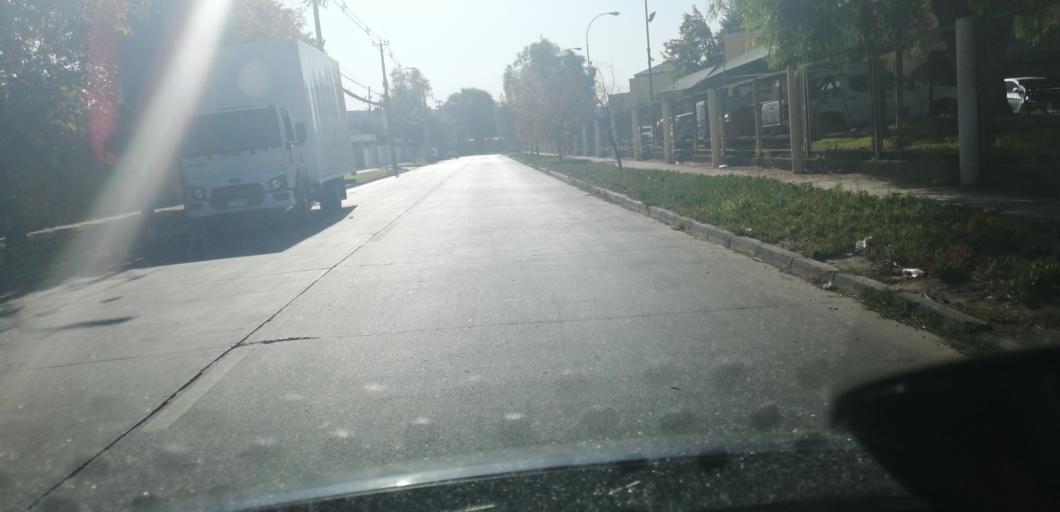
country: CL
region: Santiago Metropolitan
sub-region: Provincia de Santiago
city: Lo Prado
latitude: -33.3763
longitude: -70.7591
